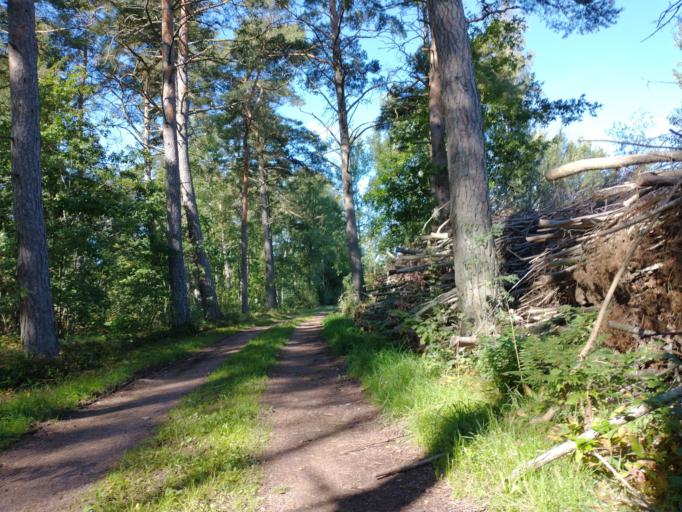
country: SE
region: Kalmar
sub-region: Kalmar Kommun
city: Lindsdal
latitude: 56.7858
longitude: 16.2851
